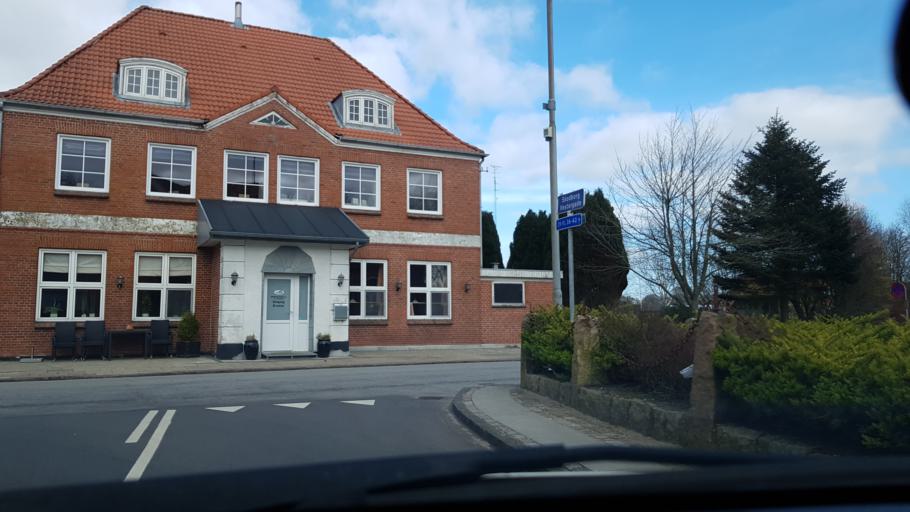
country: DK
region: South Denmark
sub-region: Vejen Kommune
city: Vejen
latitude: 55.4208
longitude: 9.1461
